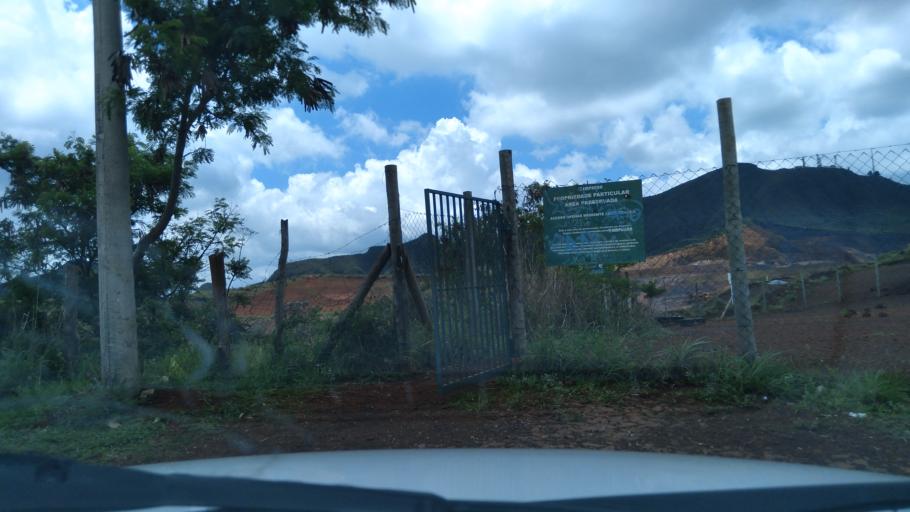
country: BR
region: Minas Gerais
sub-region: Belo Horizonte
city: Belo Horizonte
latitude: -19.9334
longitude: -43.8846
